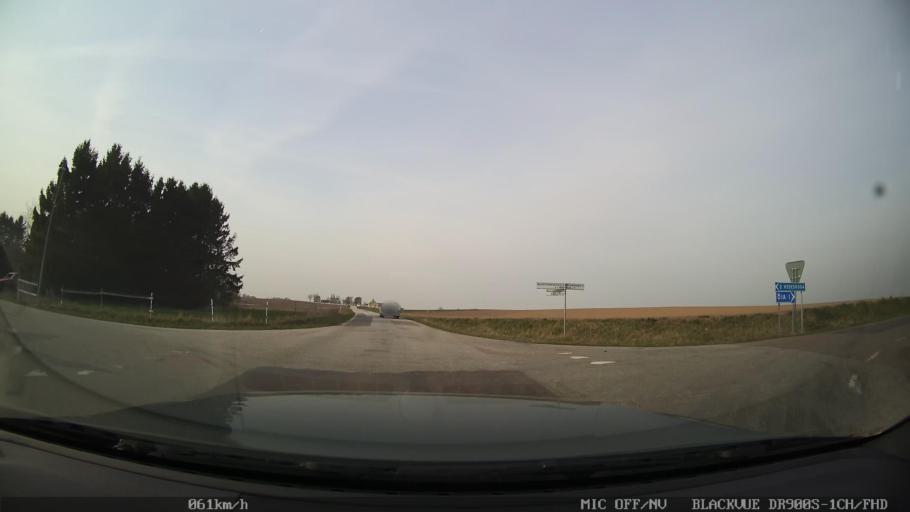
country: SE
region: Skane
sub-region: Ystads Kommun
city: Ystad
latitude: 55.4543
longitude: 13.8303
